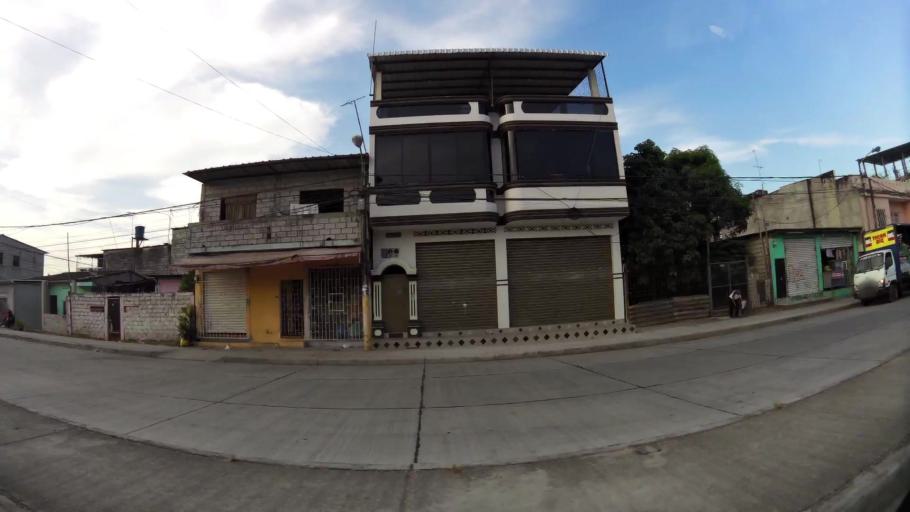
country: EC
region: Guayas
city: Eloy Alfaro
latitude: -2.0880
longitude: -79.9031
